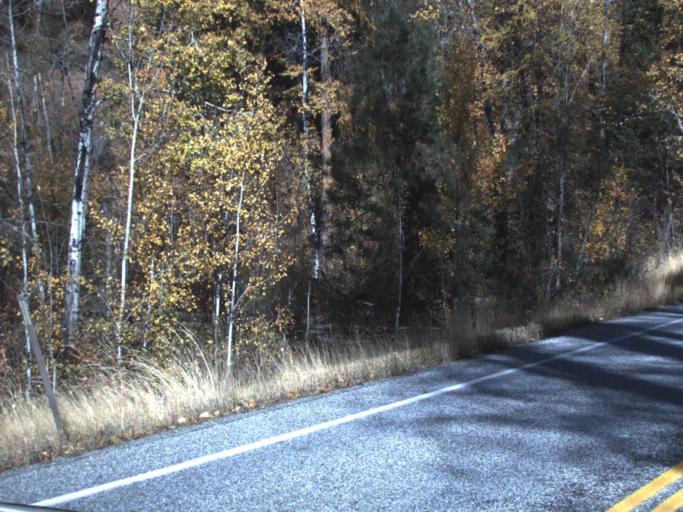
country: US
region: Washington
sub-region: Stevens County
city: Kettle Falls
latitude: 48.5898
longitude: -118.1890
